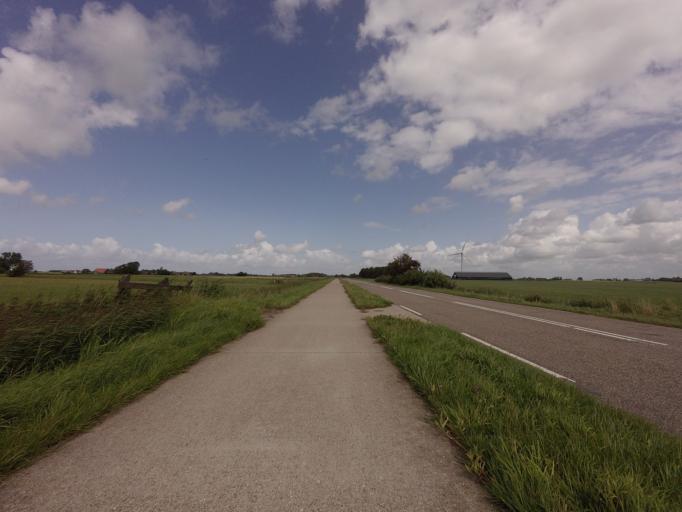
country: NL
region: Friesland
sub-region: Gemeente Harlingen
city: Harlingen
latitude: 53.1368
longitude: 5.4722
